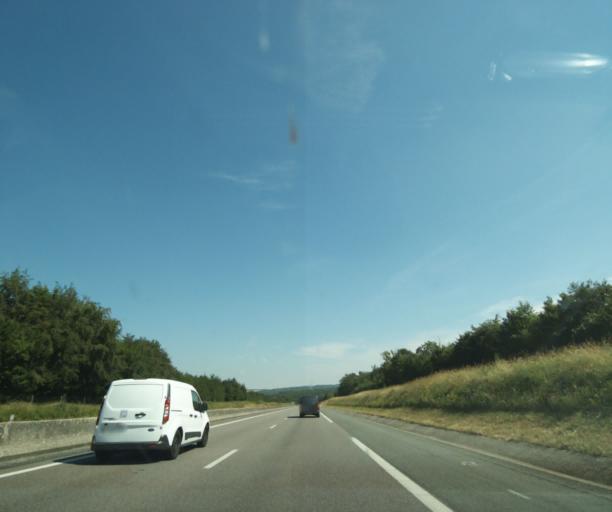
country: FR
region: Lorraine
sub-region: Departement de Meurthe-et-Moselle
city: Colombey-les-Belles
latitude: 48.4501
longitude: 5.8678
